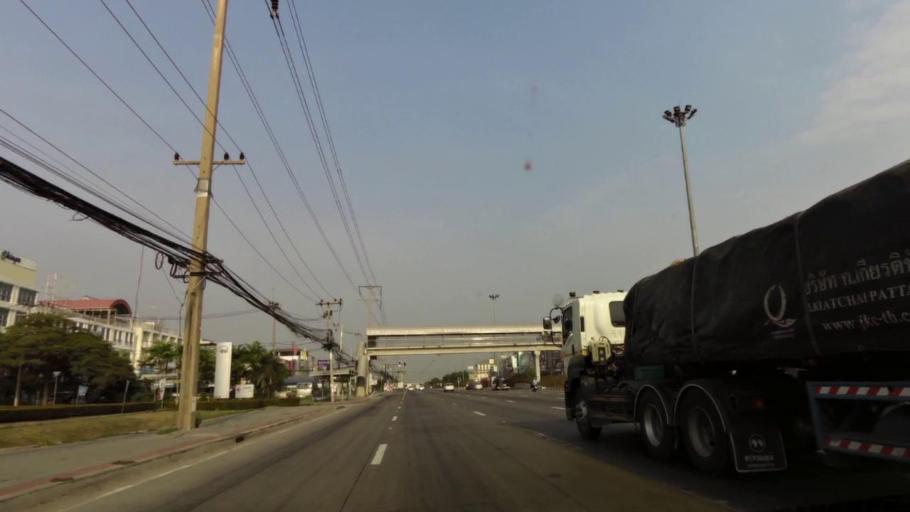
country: TH
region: Phra Nakhon Si Ayutthaya
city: Uthai
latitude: 14.3226
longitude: 100.6307
